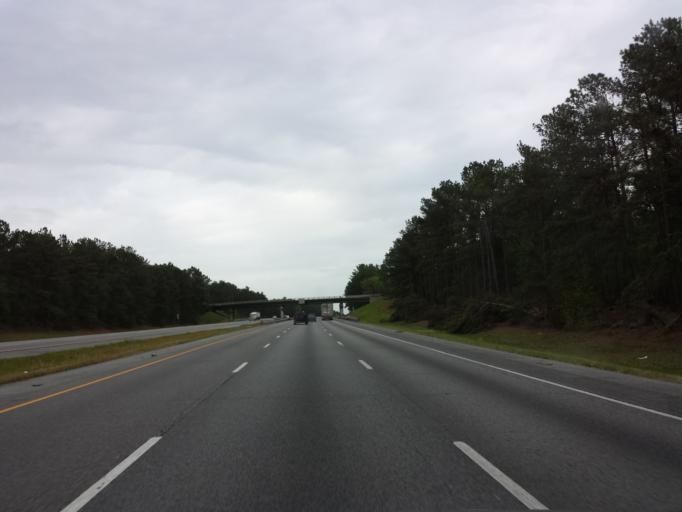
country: US
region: Georgia
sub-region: Houston County
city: Perry
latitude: 32.3803
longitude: -83.7679
